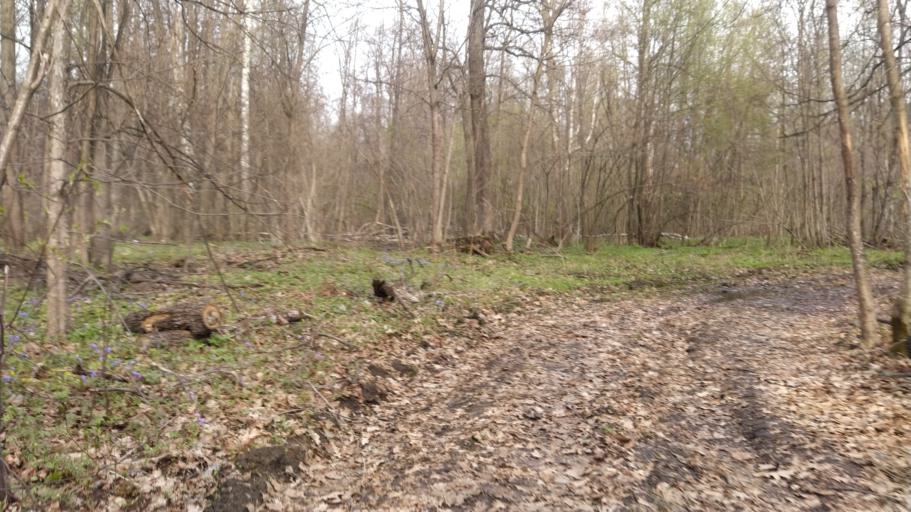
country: RU
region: Chuvashia
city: Novyye Lapsary
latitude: 56.1365
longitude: 47.1197
